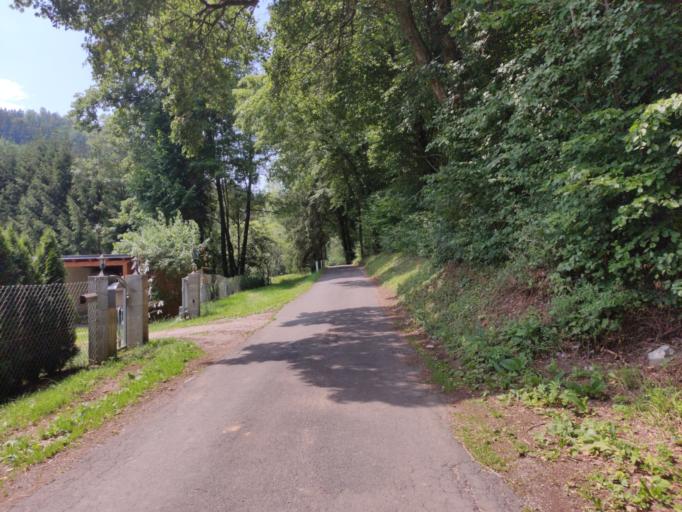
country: AT
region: Styria
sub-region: Politischer Bezirk Graz-Umgebung
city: Gratwein
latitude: 47.1264
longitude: 15.3016
